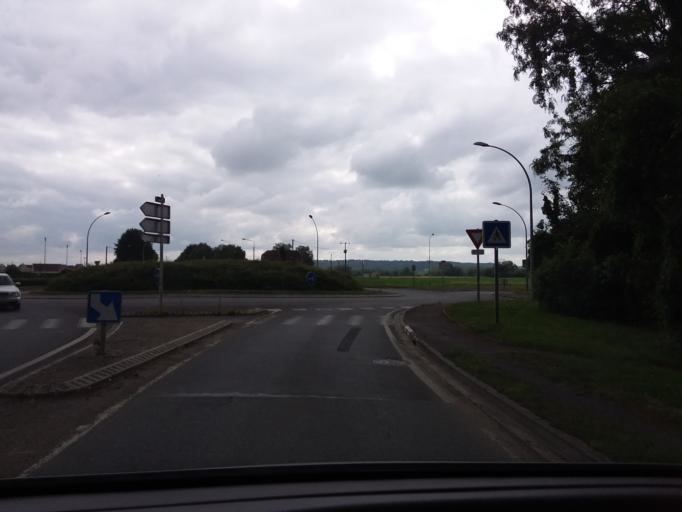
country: FR
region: Picardie
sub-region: Departement de l'Aisne
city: Bucy-le-Long
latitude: 49.3878
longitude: 3.3925
